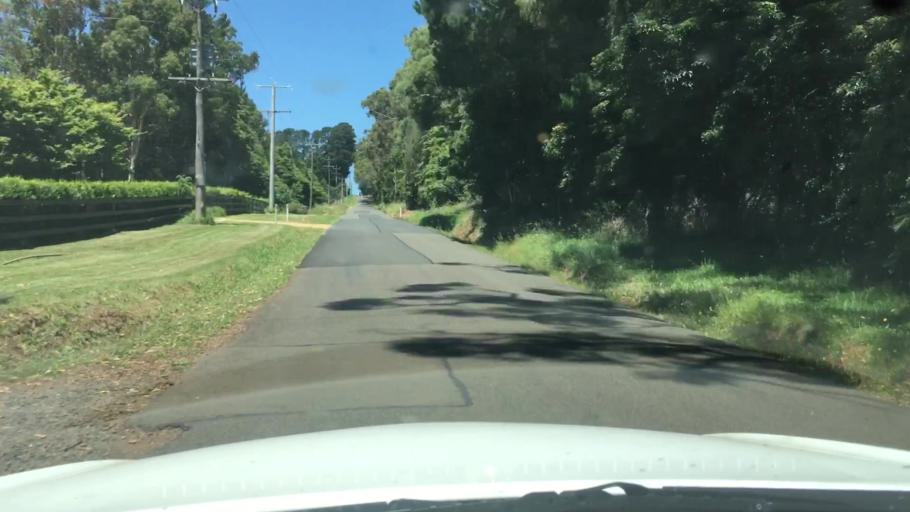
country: AU
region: Victoria
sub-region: Yarra Ranges
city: Mount Evelyn
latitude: -37.8041
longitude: 145.4210
